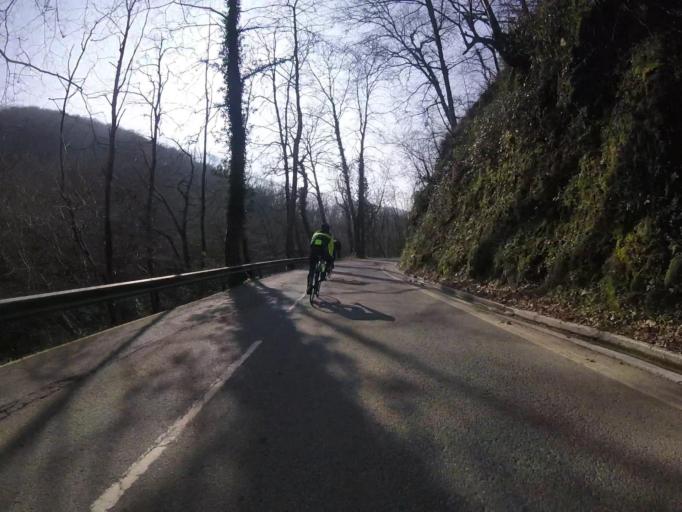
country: ES
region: Navarre
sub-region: Provincia de Navarra
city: Bera
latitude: 43.2880
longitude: -1.6798
